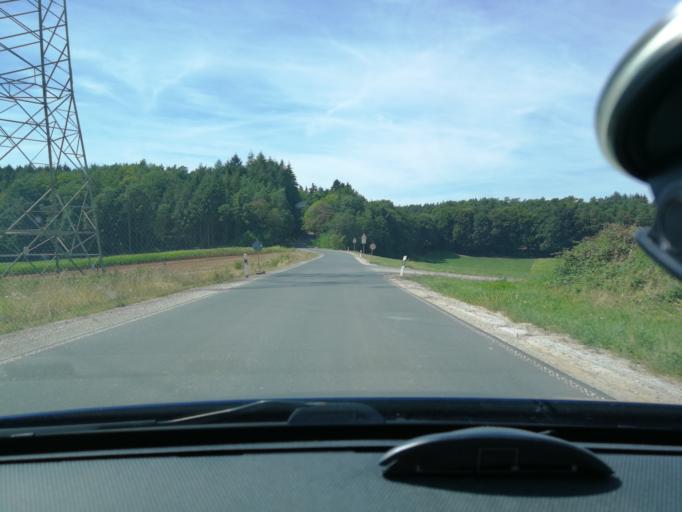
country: DE
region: Rheinland-Pfalz
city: Gladbach
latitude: 49.9226
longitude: 6.7724
